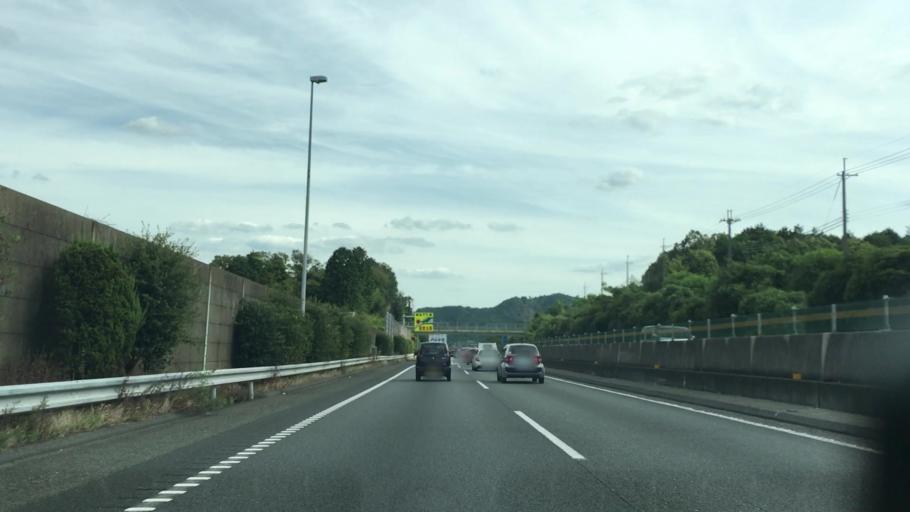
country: JP
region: Shiga Prefecture
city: Otsu-shi
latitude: 34.9847
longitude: 135.8800
